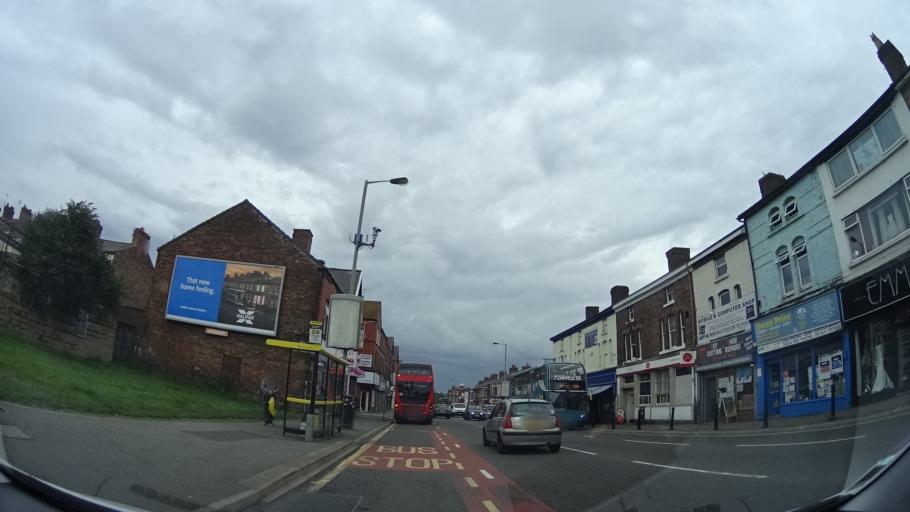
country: GB
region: England
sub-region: Liverpool
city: Liverpool
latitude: 53.4141
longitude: -2.9153
